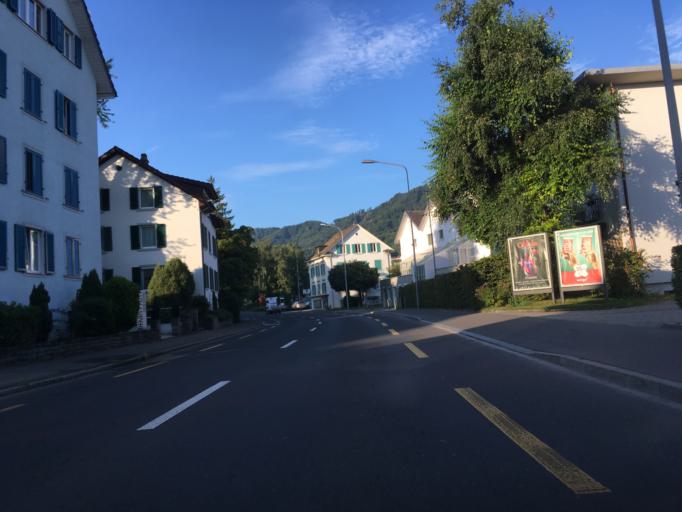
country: CH
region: Zurich
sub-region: Bezirk Horgen
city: Adliswil / Adliswil (Stadtkern)
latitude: 47.3141
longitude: 8.5285
